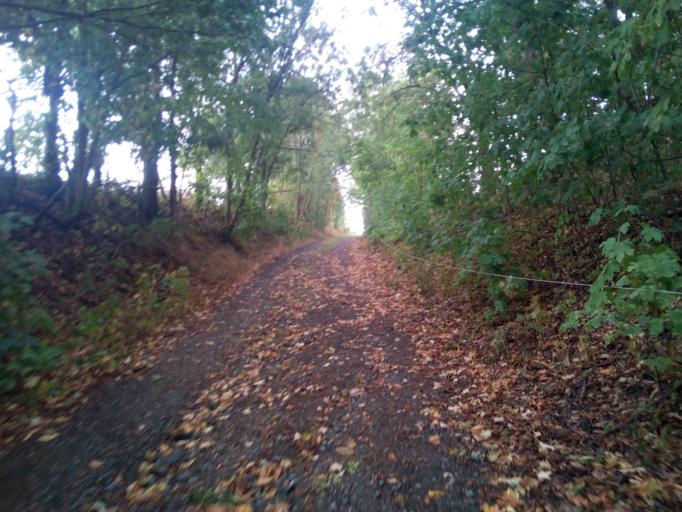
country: DE
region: Saxony
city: Kreischa
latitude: 50.9280
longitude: 13.7943
